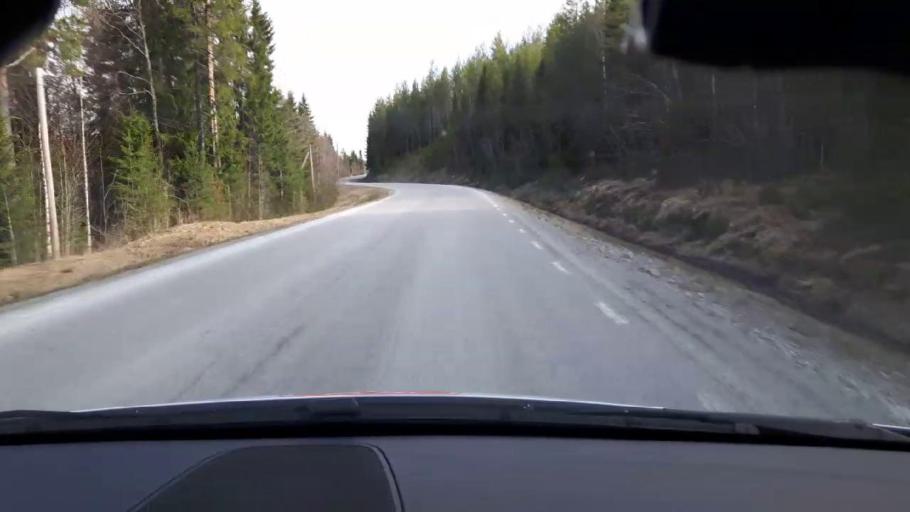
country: SE
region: Jaemtland
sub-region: Bergs Kommun
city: Hoverberg
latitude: 62.7428
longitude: 14.5825
